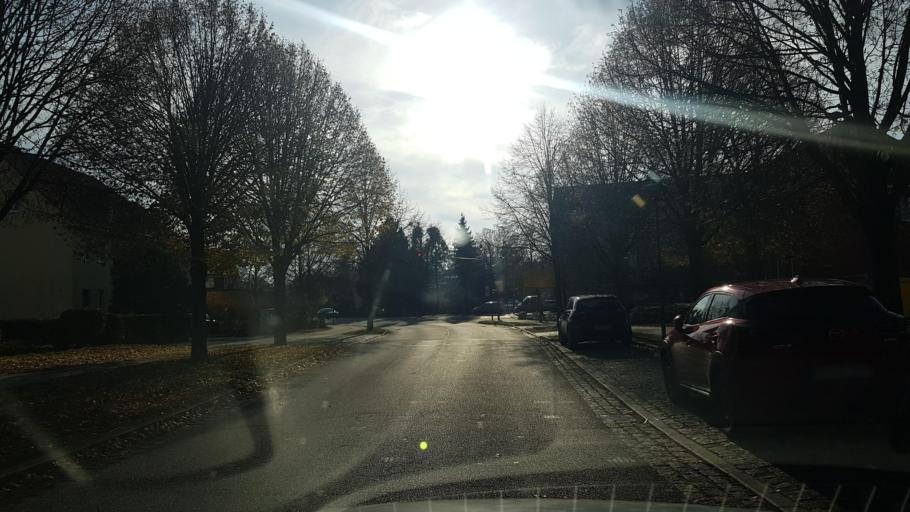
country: DE
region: Brandenburg
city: Brussow
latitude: 53.4537
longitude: 14.2151
